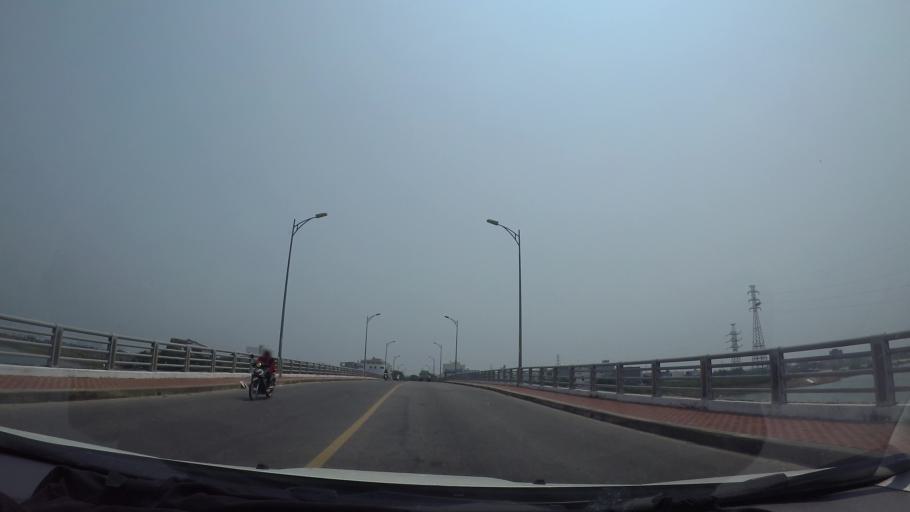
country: VN
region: Da Nang
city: Cam Le
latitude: 16.0244
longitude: 108.2232
